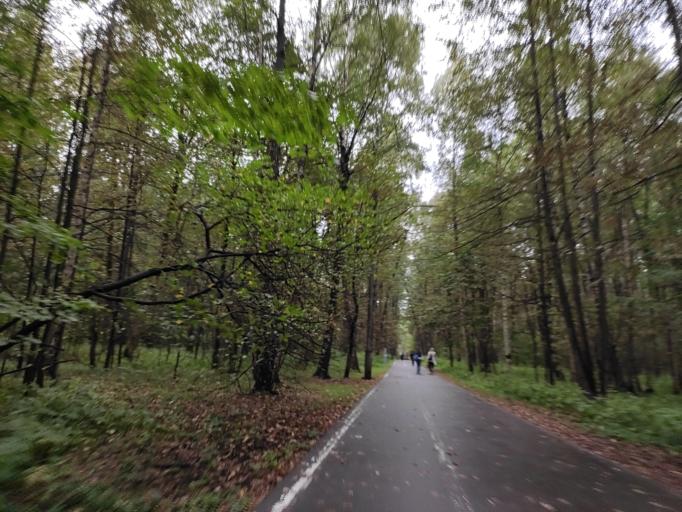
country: RU
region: Moskovskaya
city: Izmaylovo
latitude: 55.7703
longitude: 37.7834
